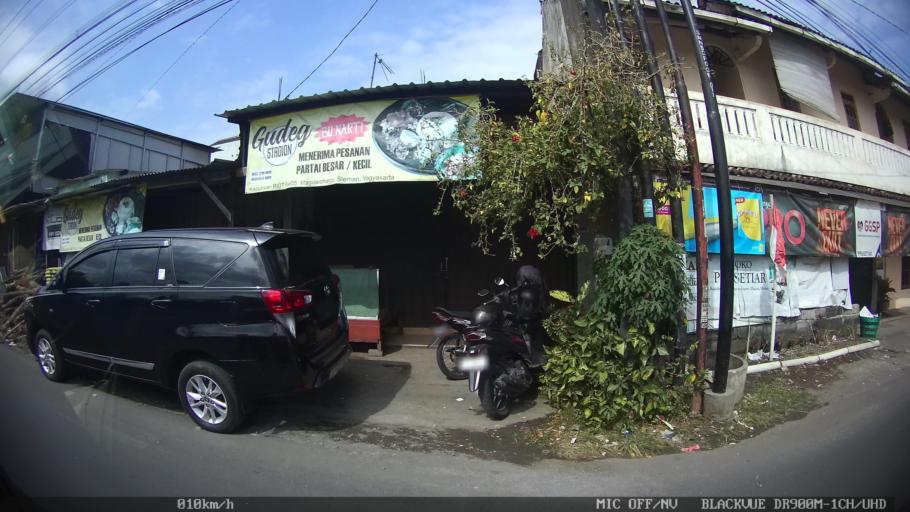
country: ID
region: Daerah Istimewa Yogyakarta
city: Depok
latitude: -7.7525
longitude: 110.4196
